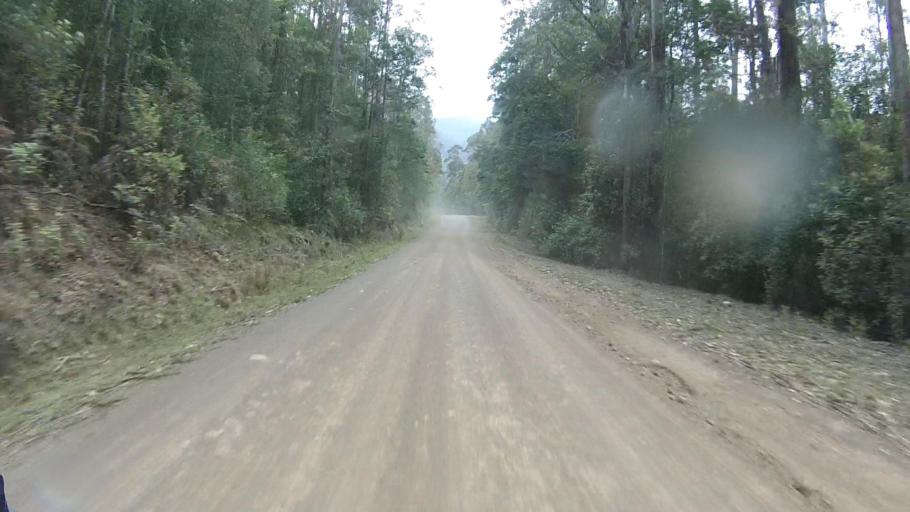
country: AU
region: Tasmania
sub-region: Sorell
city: Sorell
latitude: -42.7077
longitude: 147.8413
